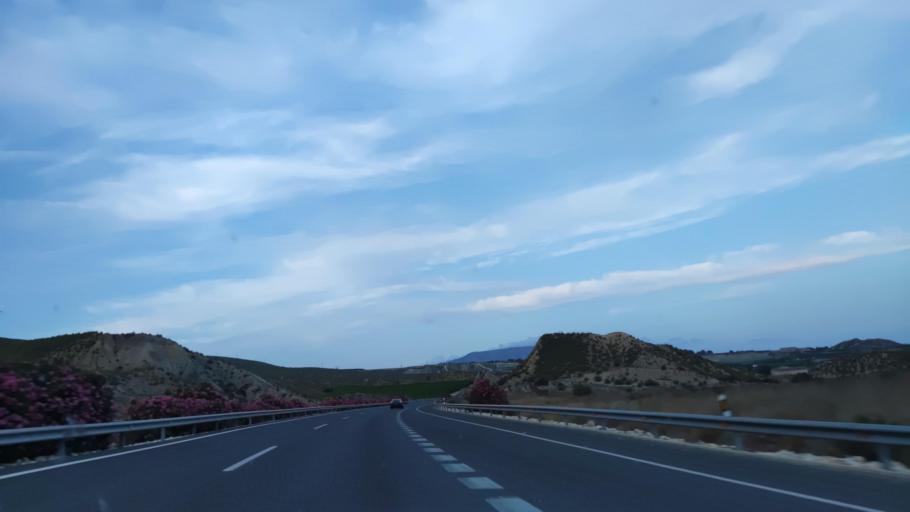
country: ES
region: Murcia
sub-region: Murcia
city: Cieza
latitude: 38.2498
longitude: -1.4067
